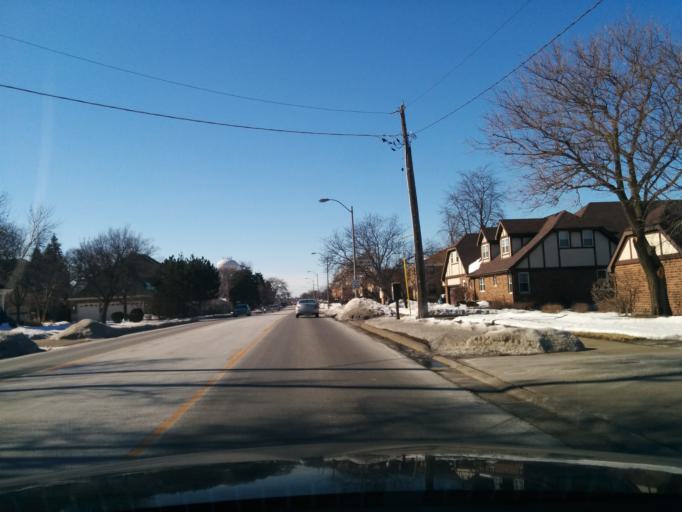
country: US
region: Illinois
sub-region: DuPage County
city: Elmhurst
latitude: 41.8903
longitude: -87.9550
